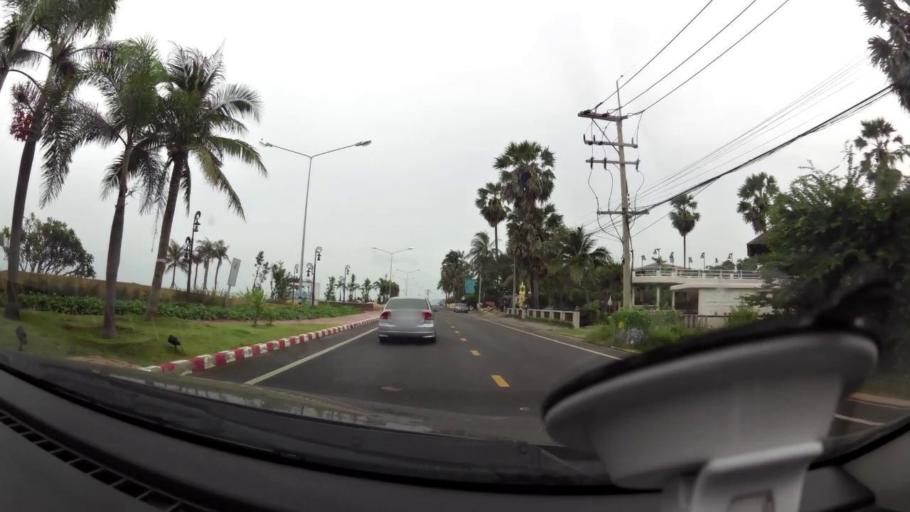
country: TH
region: Prachuap Khiri Khan
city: Pran Buri
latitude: 12.3789
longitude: 100.0000
